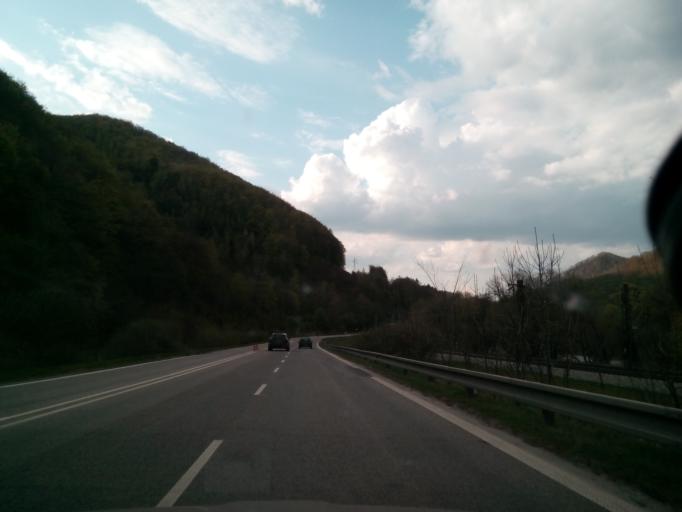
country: SK
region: Zilinsky
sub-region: Okres Zilina
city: Vrutky
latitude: 49.1424
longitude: 18.8914
